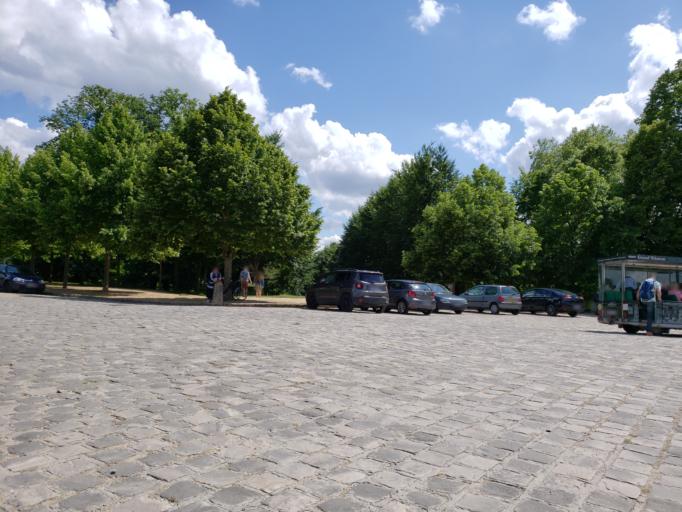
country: FR
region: Ile-de-France
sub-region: Departement des Yvelines
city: Le Chesnay
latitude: 48.8140
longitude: 2.1065
